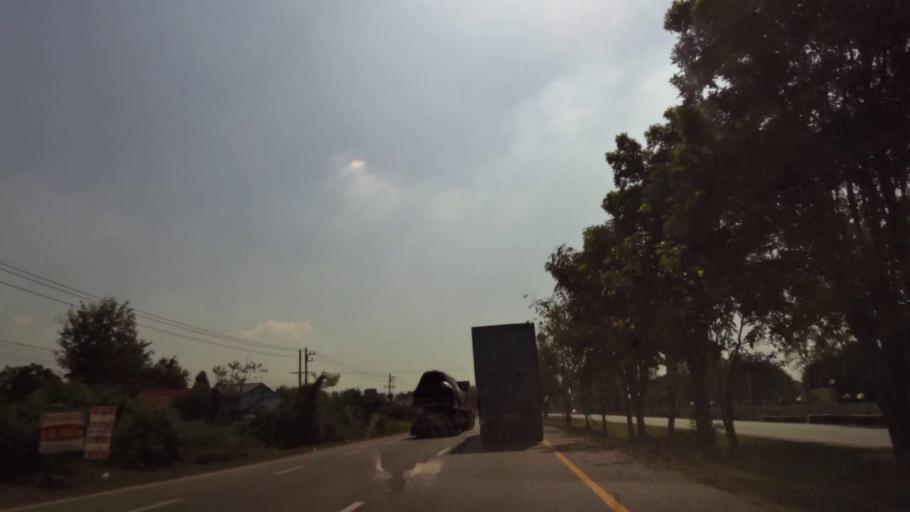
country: TH
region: Phichit
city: Bueng Na Rang
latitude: 16.1366
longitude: 100.1255
